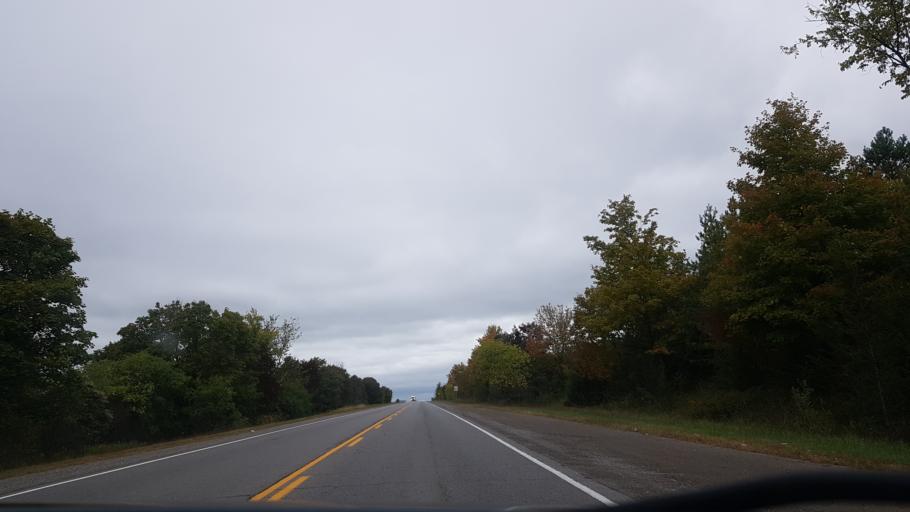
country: CA
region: Ontario
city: Peterborough
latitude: 44.2622
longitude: -78.3730
